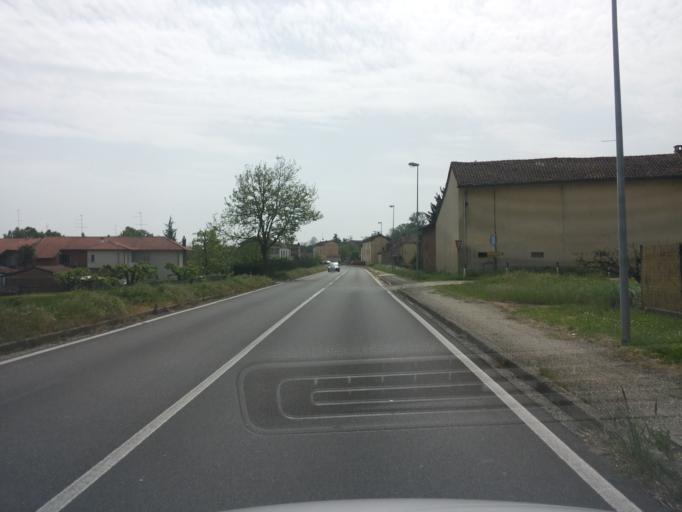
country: IT
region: Piedmont
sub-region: Provincia di Alessandria
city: Terruggia
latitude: 45.0913
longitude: 8.4629
